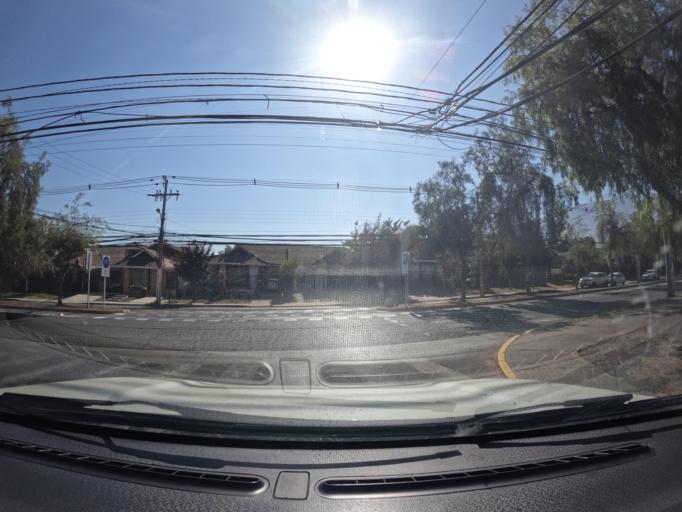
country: CL
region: Santiago Metropolitan
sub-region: Provincia de Santiago
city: Villa Presidente Frei, Nunoa, Santiago, Chile
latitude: -33.4805
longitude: -70.5535
